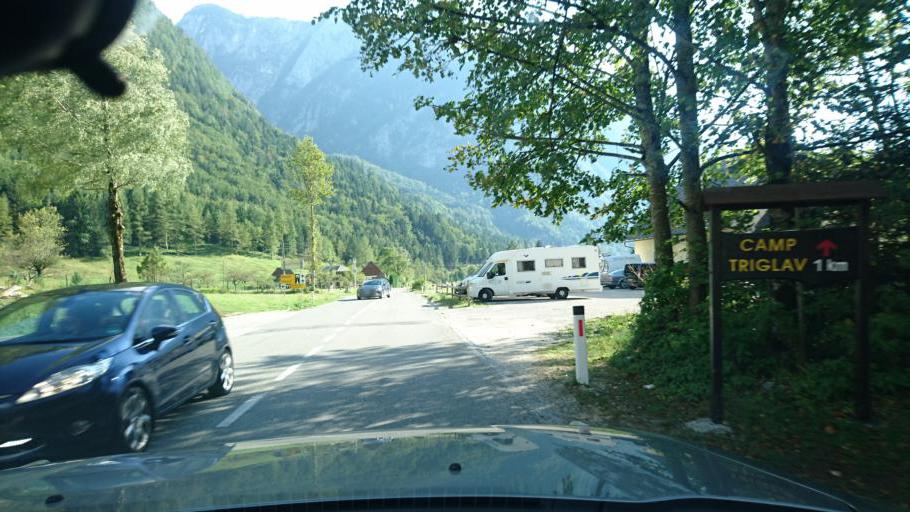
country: SI
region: Kranjska Gora
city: Kranjska Gora
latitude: 46.3805
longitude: 13.7513
